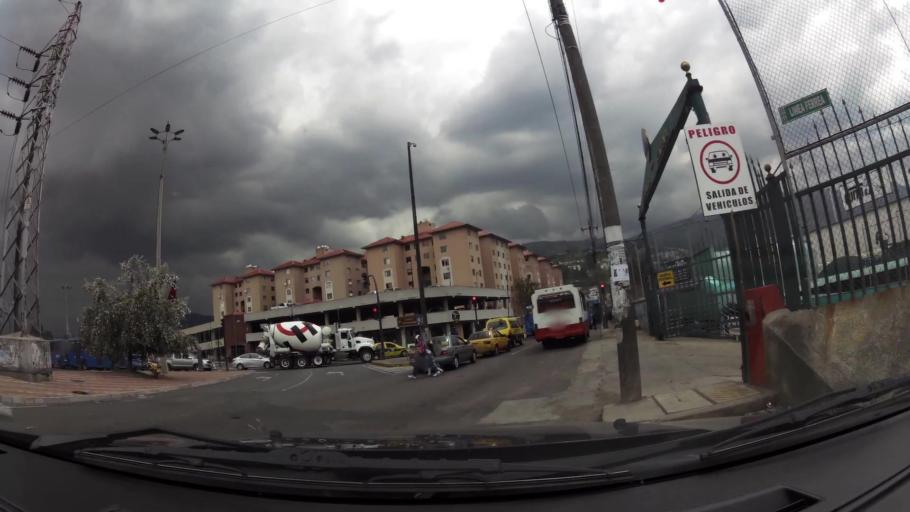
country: EC
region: Pichincha
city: Quito
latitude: -0.2366
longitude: -78.5079
